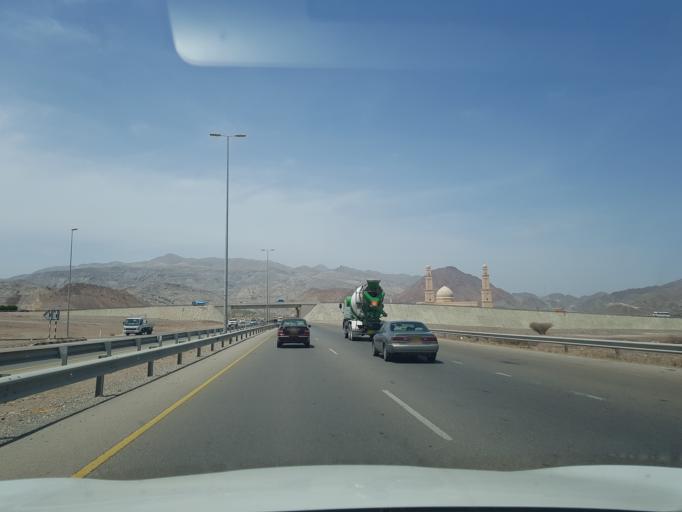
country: OM
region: Muhafazat ad Dakhiliyah
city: Bidbid
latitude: 23.4662
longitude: 58.1293
